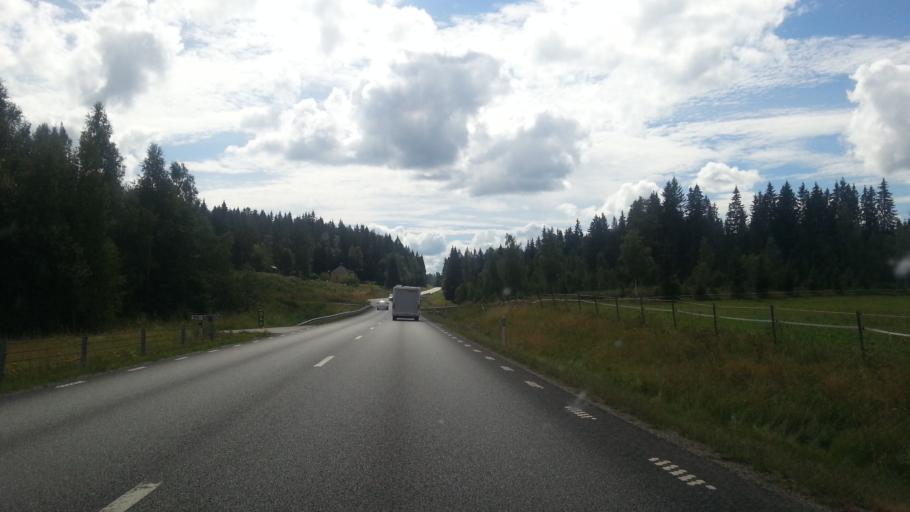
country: SE
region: OErebro
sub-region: Lindesbergs Kommun
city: Stora
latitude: 59.6797
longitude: 15.0990
